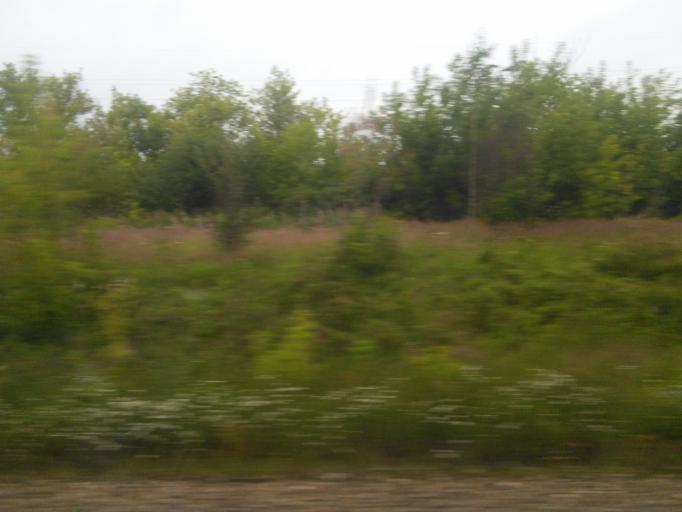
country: RU
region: Moskovskaya
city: Mozhaysk
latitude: 55.4953
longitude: 36.0777
